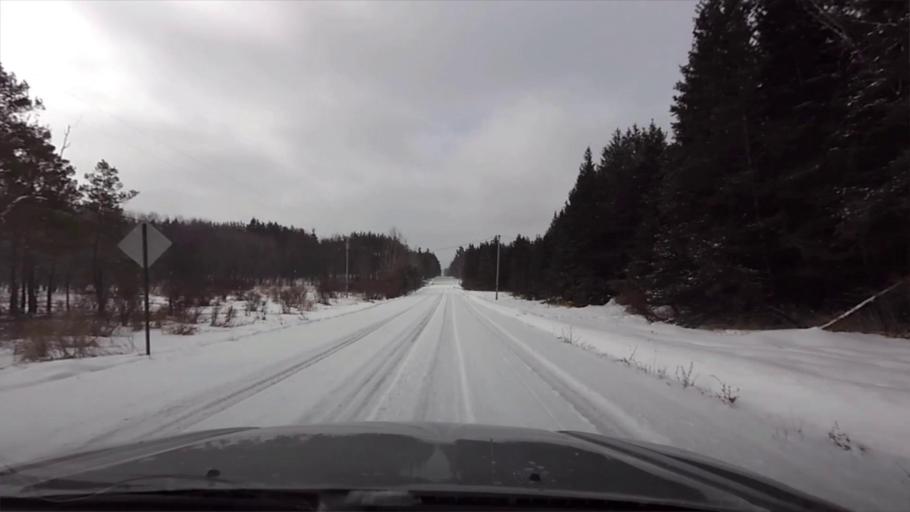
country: US
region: New York
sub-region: Cattaraugus County
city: Franklinville
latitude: 42.3290
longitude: -78.3540
